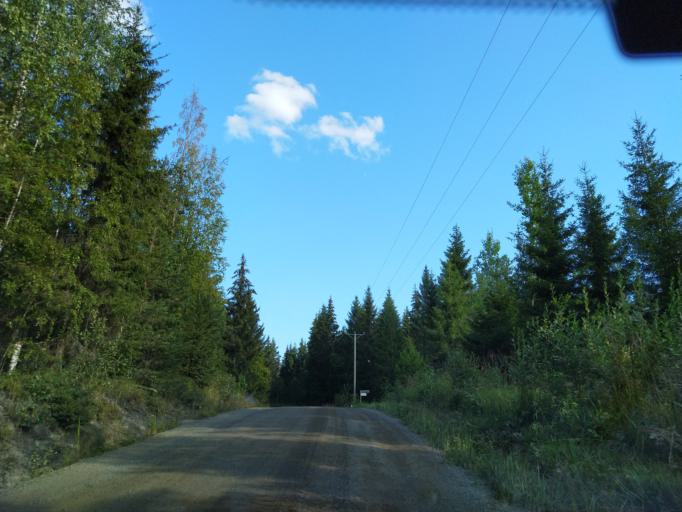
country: FI
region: Central Finland
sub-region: Jaemsae
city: Kuhmoinen
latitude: 61.6931
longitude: 24.9480
